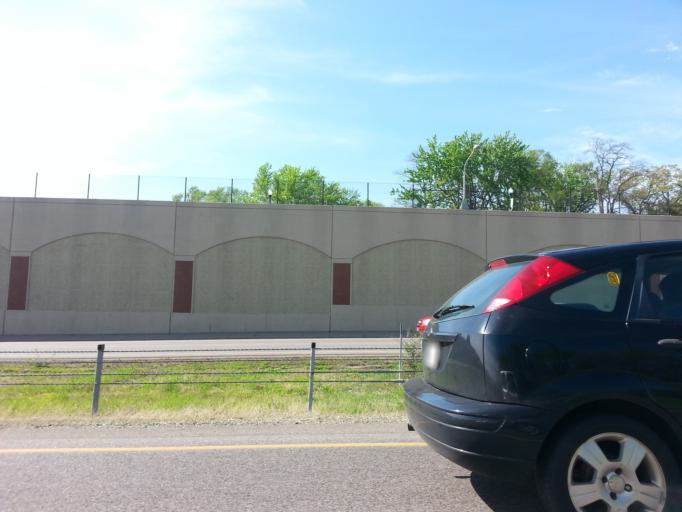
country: US
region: Minnesota
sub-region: Ramsey County
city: North Saint Paul
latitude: 45.0164
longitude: -92.9906
